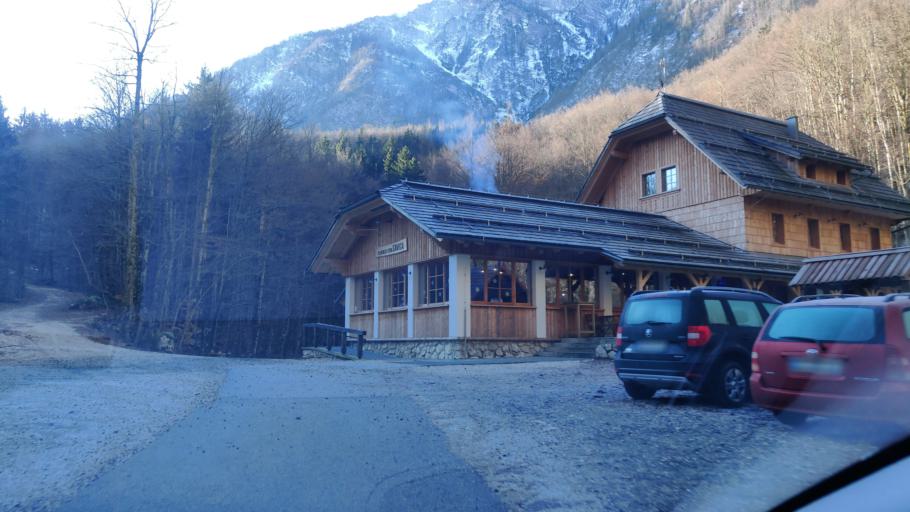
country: SI
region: Tolmin
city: Tolmin
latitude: 46.2896
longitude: 13.8020
